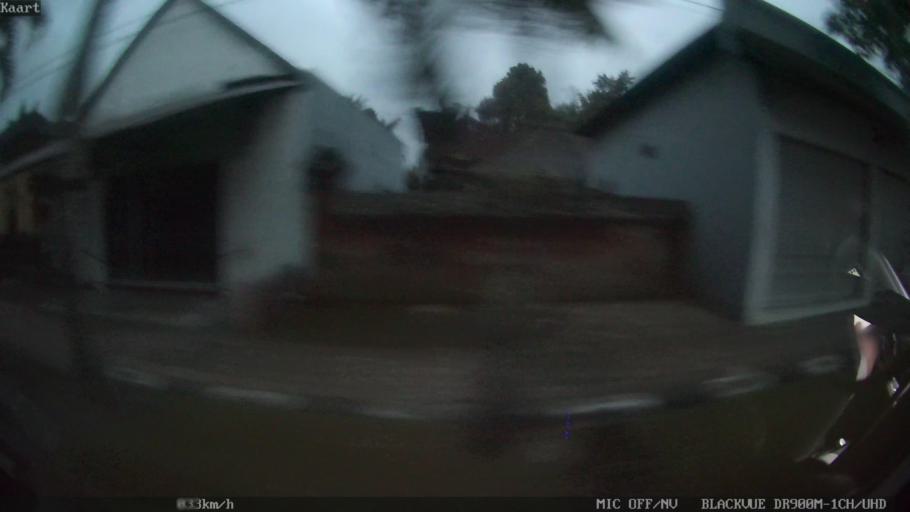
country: ID
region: Bali
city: Banjar Mambalkajanan
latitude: -8.5545
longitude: 115.2192
